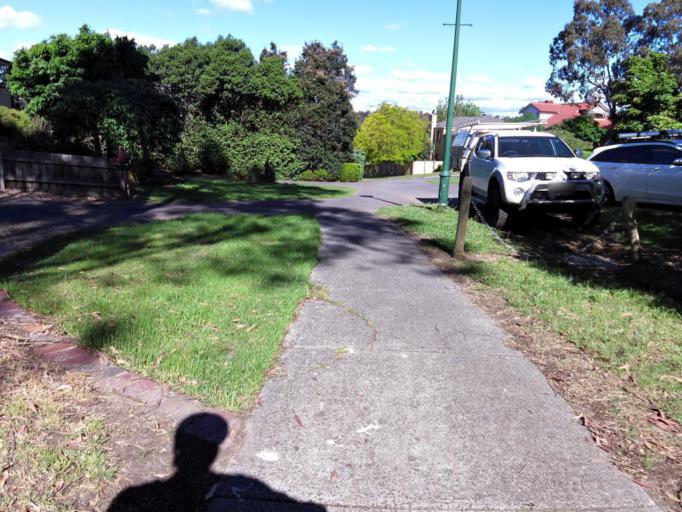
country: AU
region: Victoria
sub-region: Nillumbik
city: Eltham
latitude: -37.7285
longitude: 145.1387
